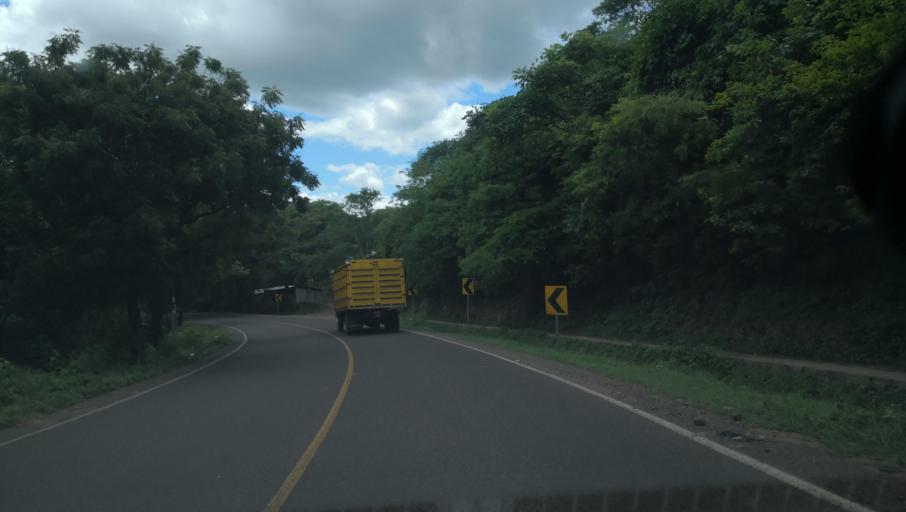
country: NI
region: Madriz
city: Yalaguina
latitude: 13.4662
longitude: -86.4708
